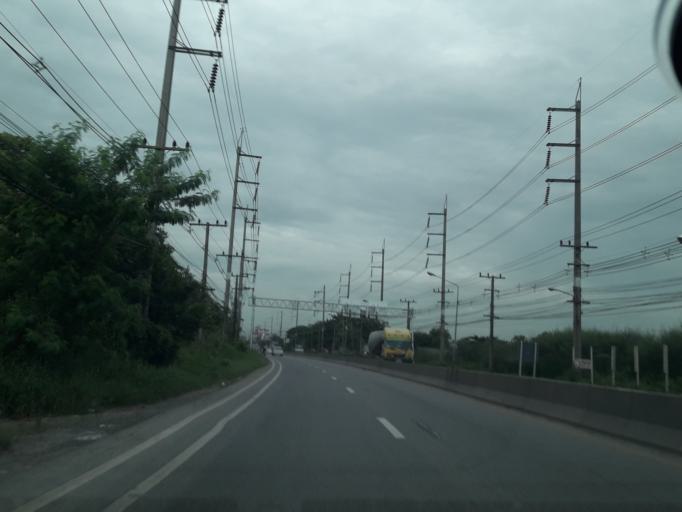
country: TH
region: Pathum Thani
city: Lam Luk Ka
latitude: 13.9400
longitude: 100.7629
